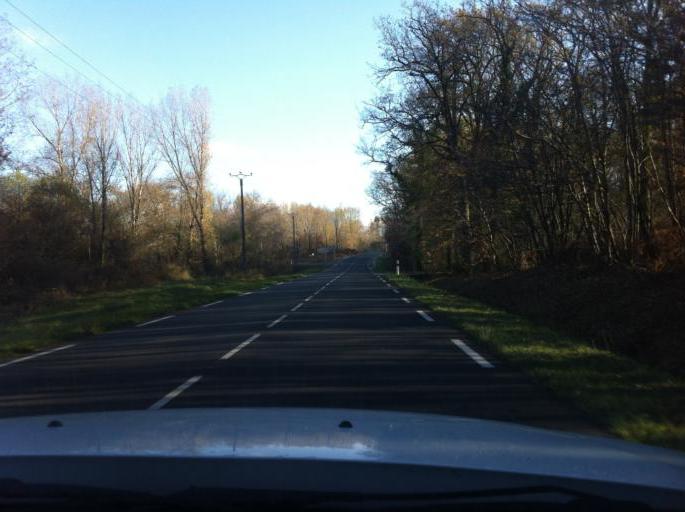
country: FR
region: Aquitaine
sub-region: Departement de la Dordogne
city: Rouffignac-Saint-Cernin-de-Reilhac
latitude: 45.0404
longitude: 0.8754
